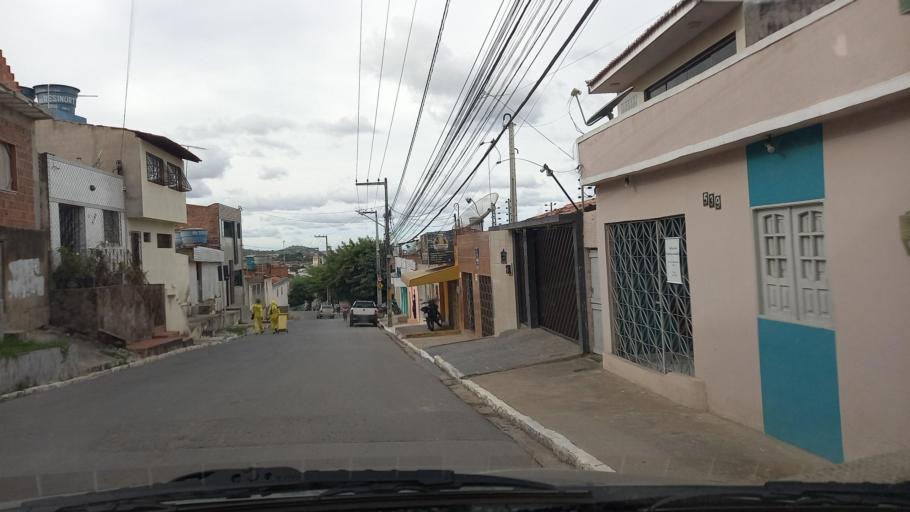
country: BR
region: Pernambuco
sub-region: Gravata
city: Gravata
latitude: -8.2093
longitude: -35.5709
